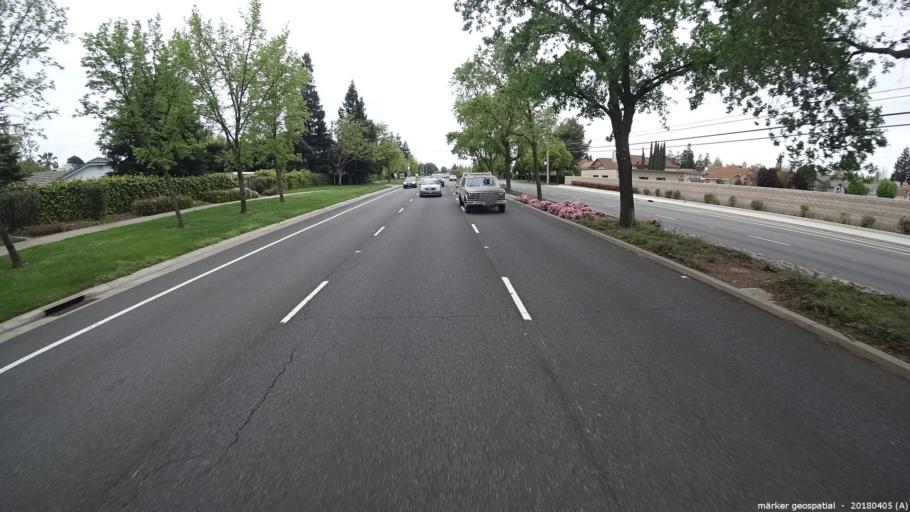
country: US
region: California
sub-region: Sacramento County
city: Laguna
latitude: 38.4274
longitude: -121.4474
